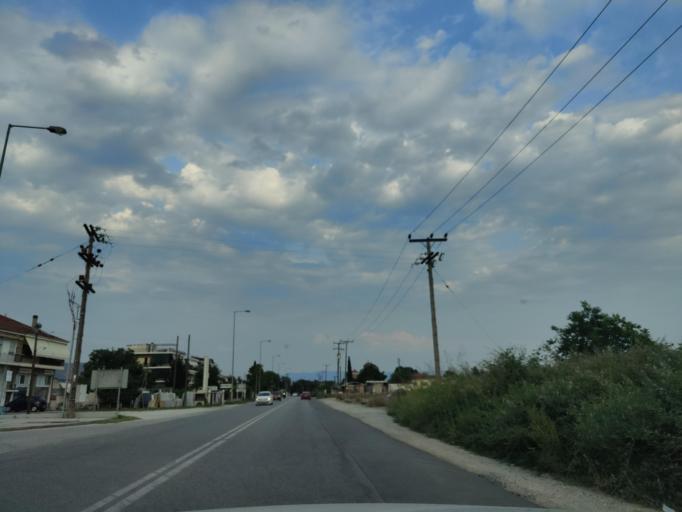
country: GR
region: East Macedonia and Thrace
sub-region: Nomos Dramas
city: Xiropotamos
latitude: 41.1557
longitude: 24.1089
